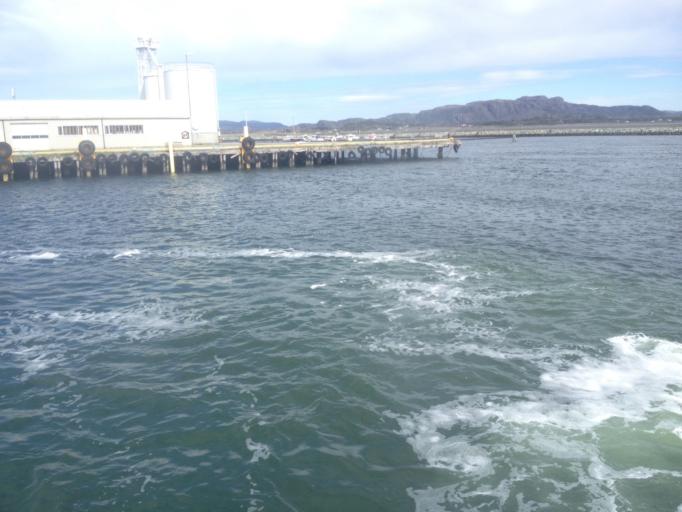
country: NO
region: Sor-Trondelag
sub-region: Orland
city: Brekstad
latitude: 63.6860
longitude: 9.6691
